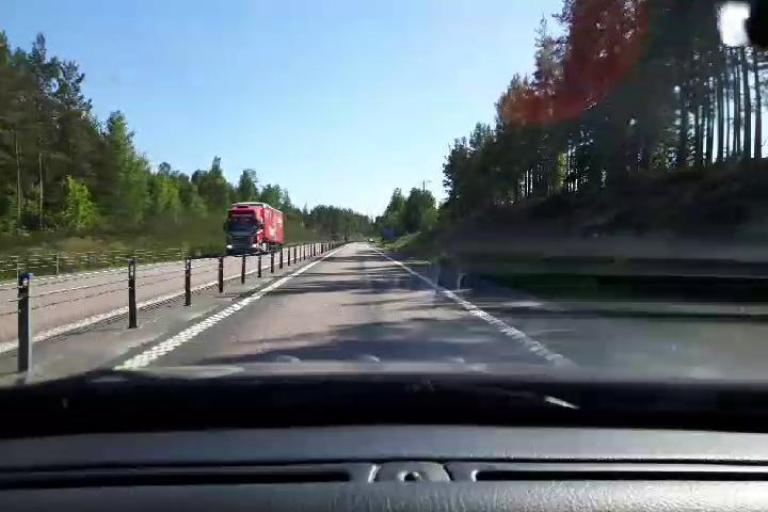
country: SE
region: Gaevleborg
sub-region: Soderhamns Kommun
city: Ljusne
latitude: 61.0836
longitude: 16.9727
